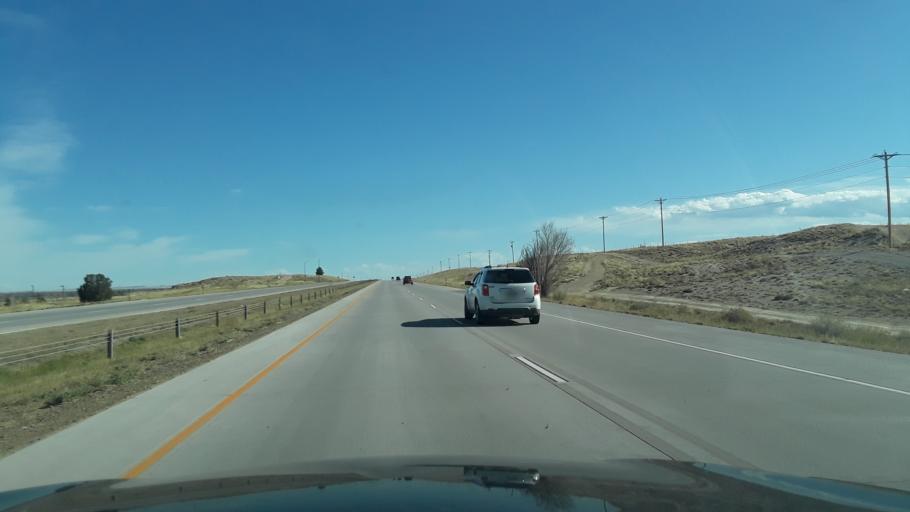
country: US
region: Colorado
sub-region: Pueblo County
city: Pueblo
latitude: 38.3030
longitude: -104.6637
